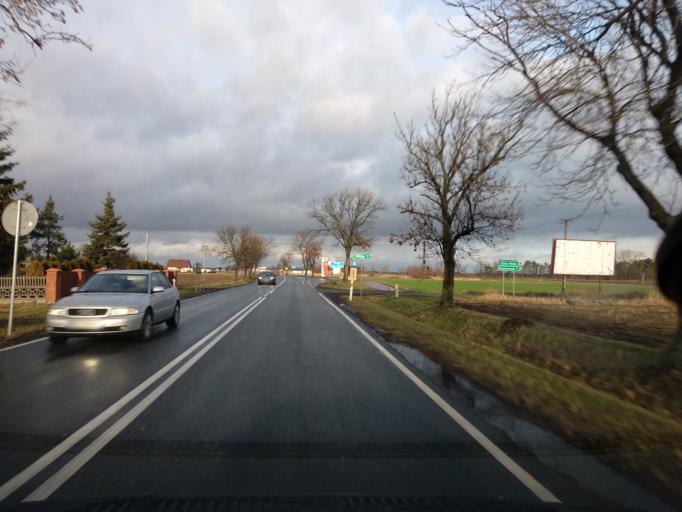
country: PL
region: Greater Poland Voivodeship
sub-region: Powiat koninski
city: Rychwal
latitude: 52.1026
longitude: 18.1671
